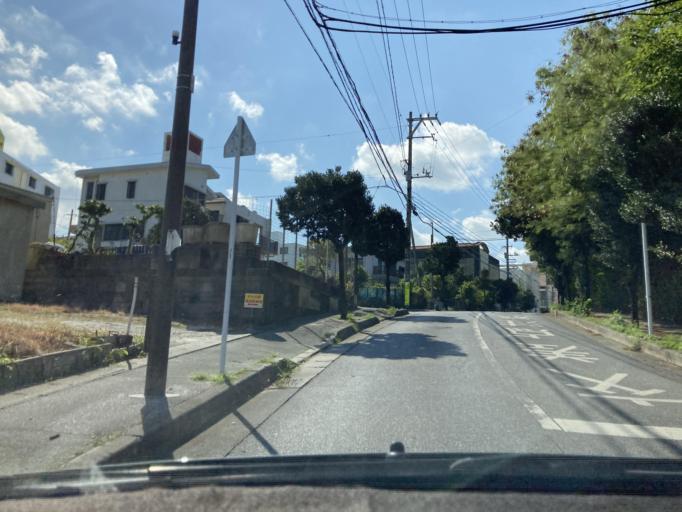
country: JP
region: Okinawa
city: Tomigusuku
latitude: 26.1814
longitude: 127.6564
